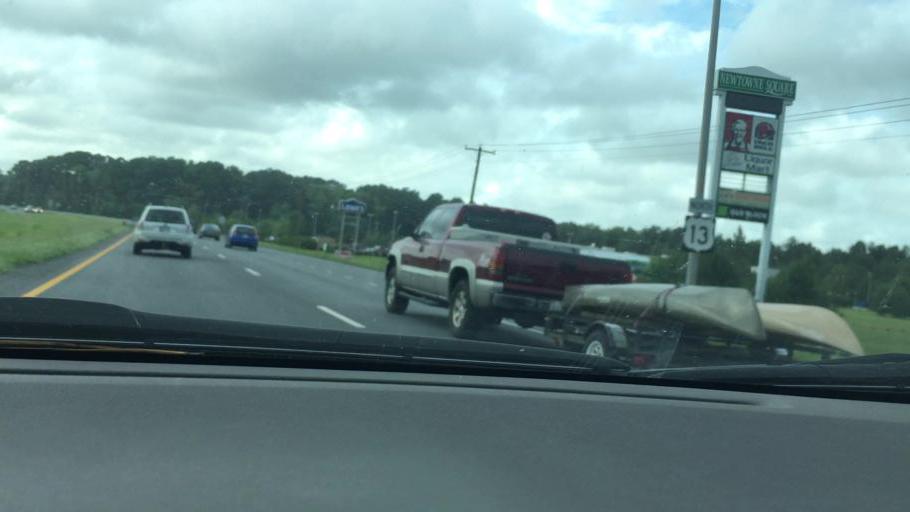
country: US
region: Maryland
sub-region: Worcester County
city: Pocomoke City
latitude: 38.0756
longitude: -75.5587
